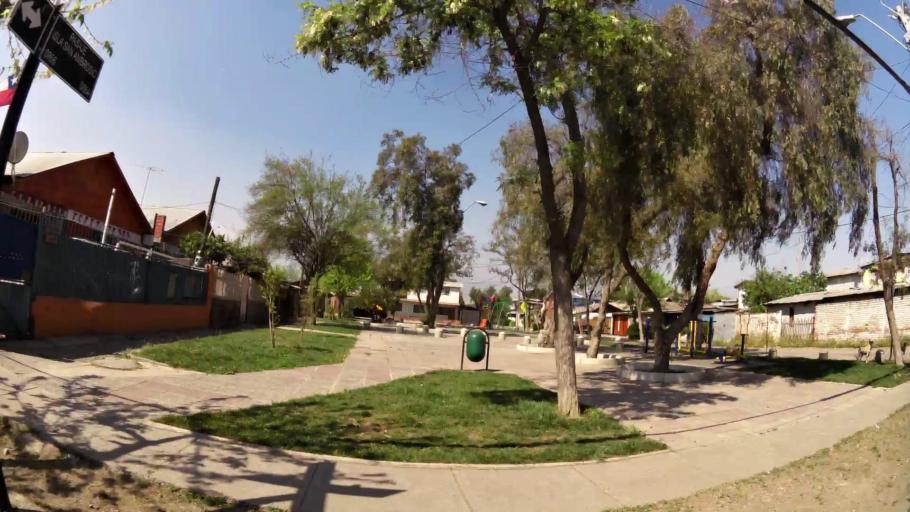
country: CL
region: Santiago Metropolitan
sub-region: Provincia de Santiago
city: La Pintana
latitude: -33.5460
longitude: -70.6125
